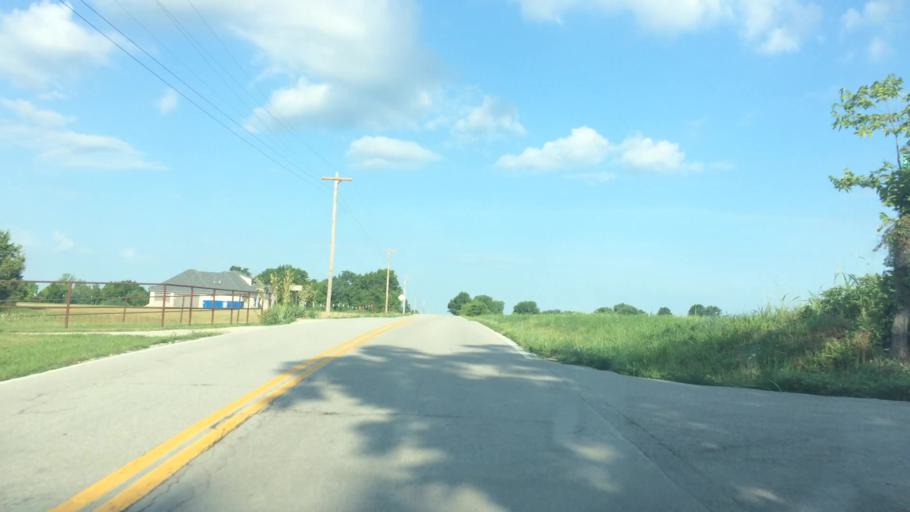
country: US
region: Missouri
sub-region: Greene County
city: Strafford
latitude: 37.2723
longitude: -93.2049
